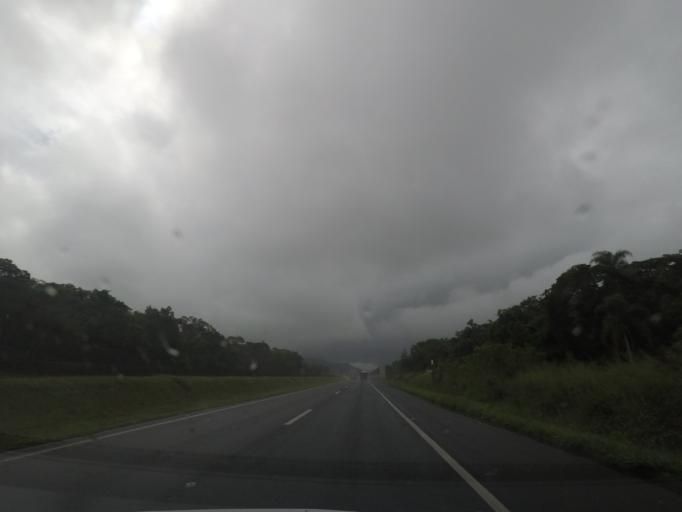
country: BR
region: Sao Paulo
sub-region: Juquia
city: Juquia
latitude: -24.3450
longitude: -47.6482
